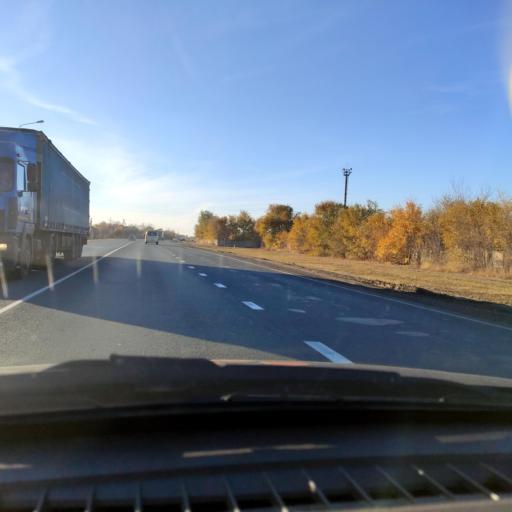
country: RU
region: Samara
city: Varlamovo
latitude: 53.1918
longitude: 48.3425
